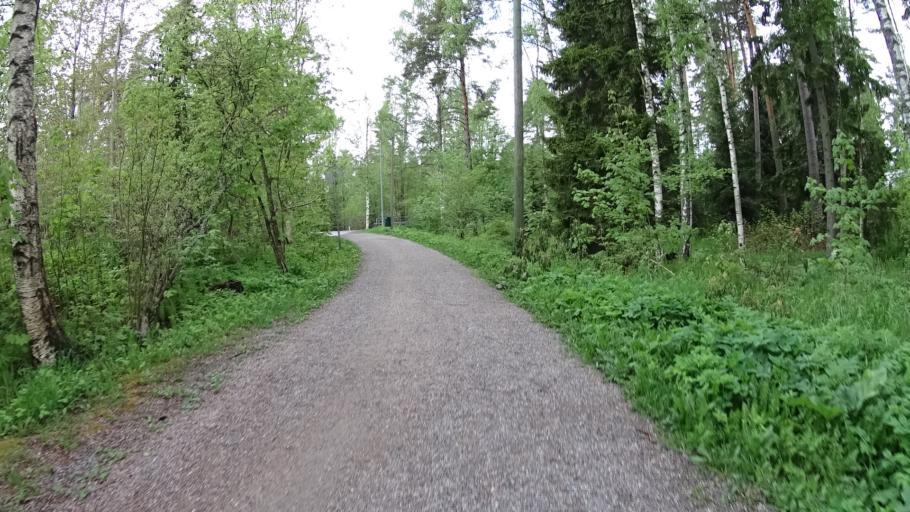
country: FI
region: Uusimaa
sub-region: Helsinki
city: Kauniainen
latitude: 60.2112
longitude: 24.7028
